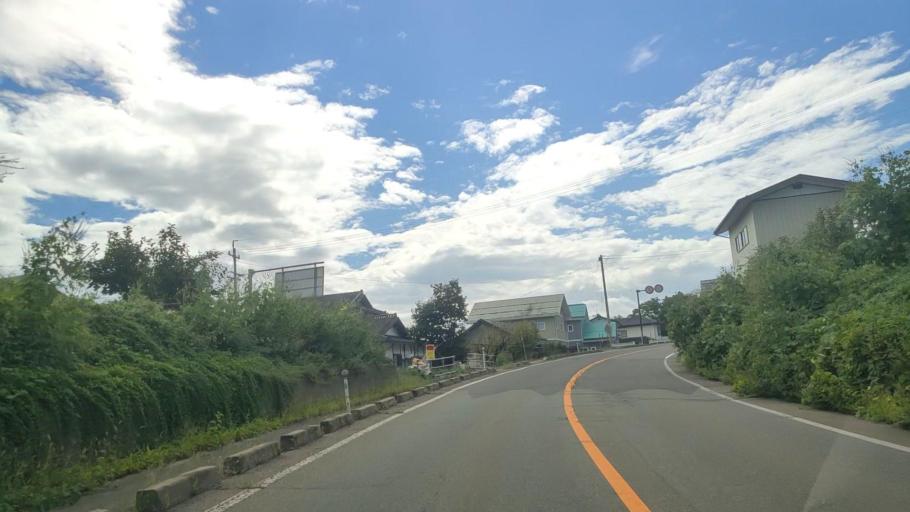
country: JP
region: Nagano
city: Nakano
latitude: 36.7552
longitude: 138.3174
